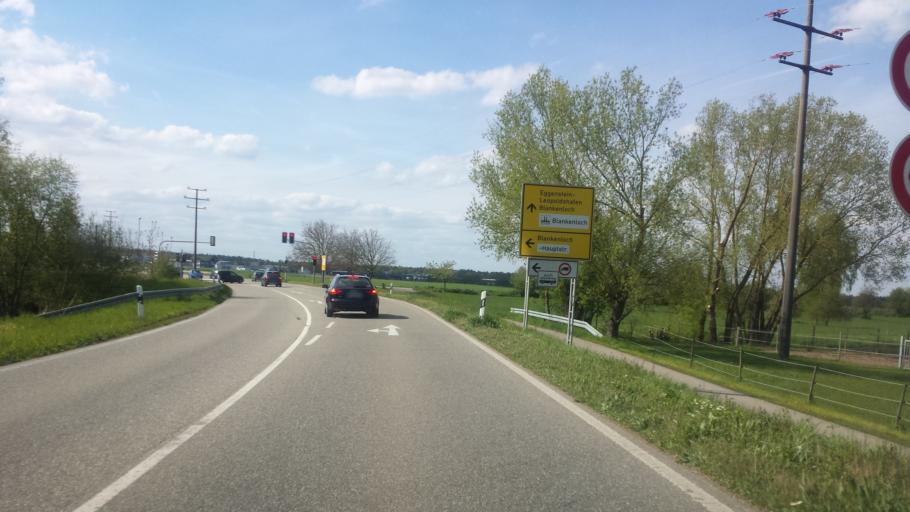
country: DE
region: Baden-Wuerttemberg
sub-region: Karlsruhe Region
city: Weingarten
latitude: 49.0710
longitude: 8.4766
